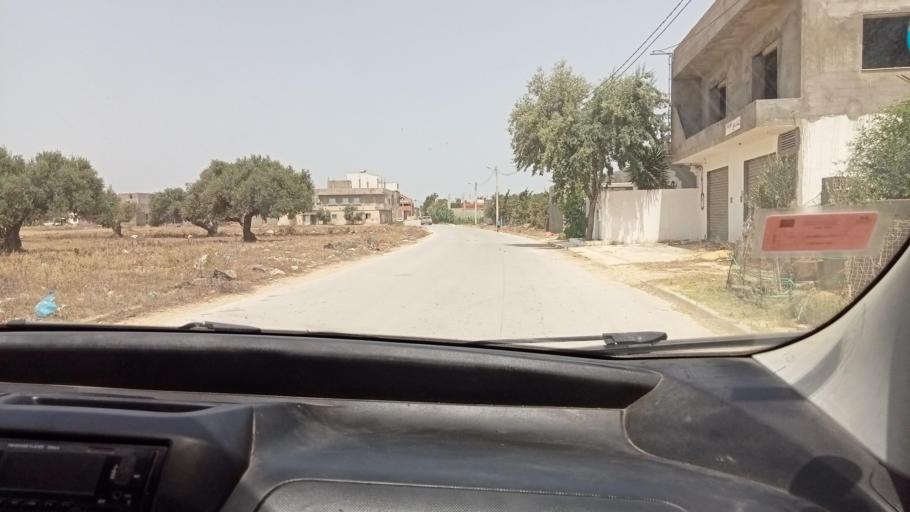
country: TN
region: Nabul
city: Qulaybiyah
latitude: 36.8616
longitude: 11.0867
